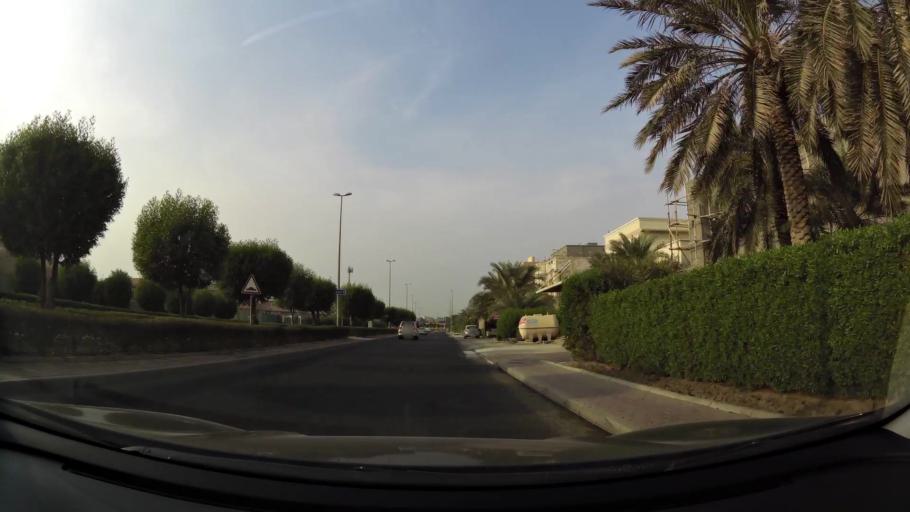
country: KW
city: Al Funaytis
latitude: 29.2194
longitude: 48.0757
